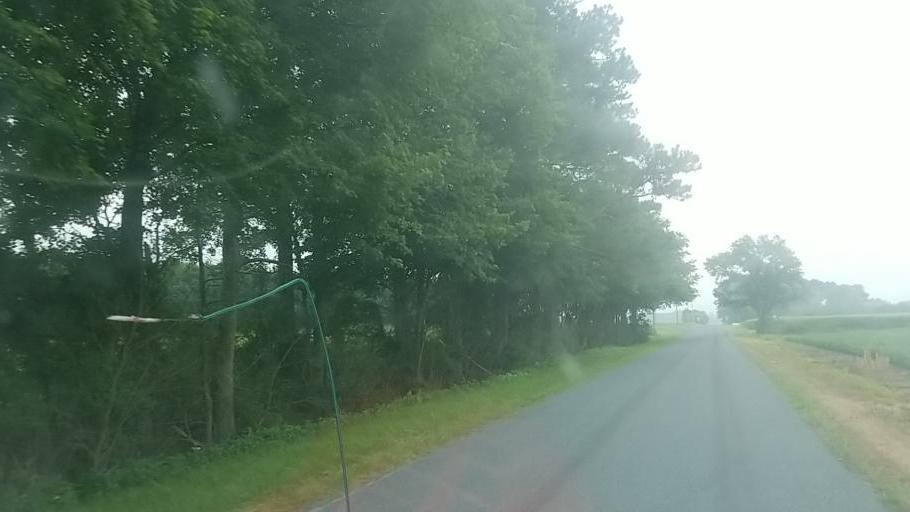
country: US
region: Maryland
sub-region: Wicomico County
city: Pittsville
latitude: 38.4521
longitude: -75.3726
